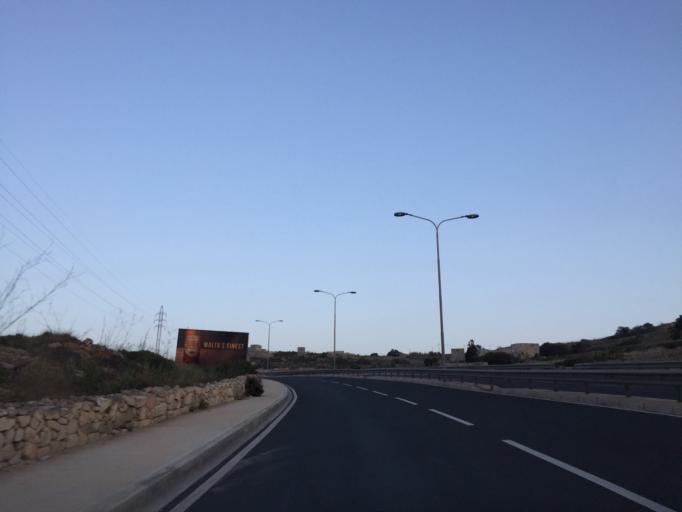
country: MT
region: Il-Mellieha
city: Mellieha
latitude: 35.9559
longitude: 14.3533
